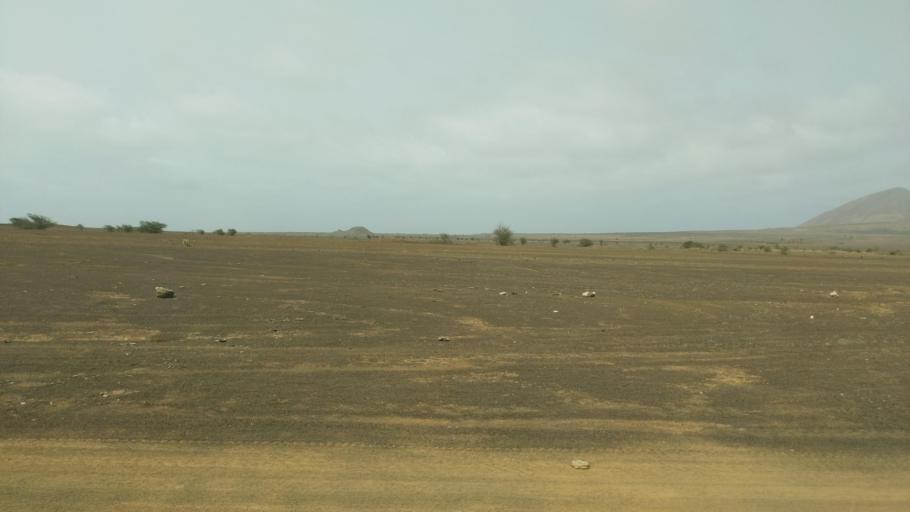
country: CV
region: Sal
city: Espargos
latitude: 16.7976
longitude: -22.9572
